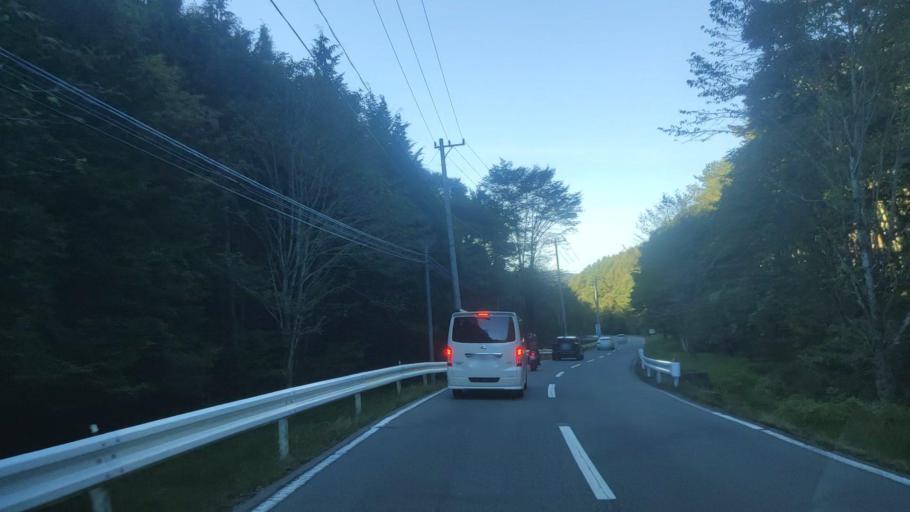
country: JP
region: Nagano
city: Kamimaruko
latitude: 36.2139
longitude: 138.2931
